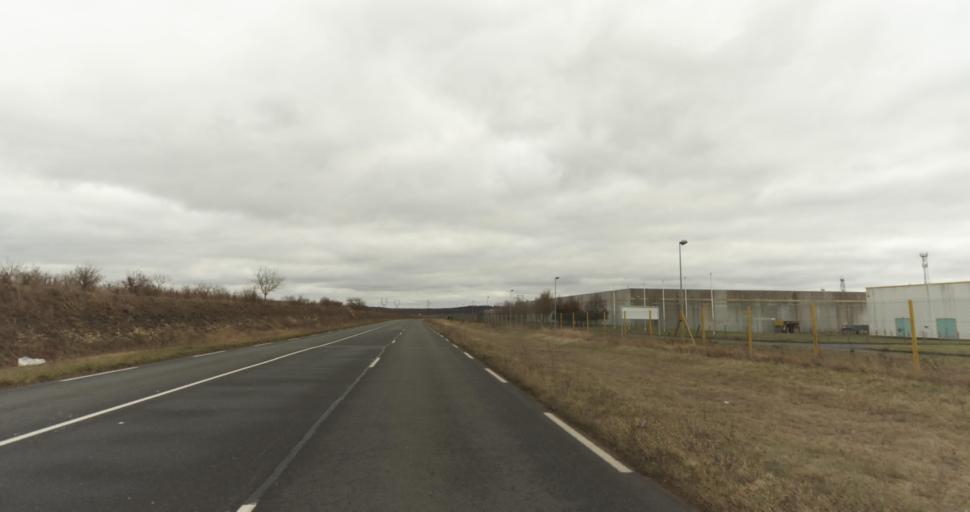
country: FR
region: Pays de la Loire
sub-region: Departement de Maine-et-Loire
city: Varrains
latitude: 47.2111
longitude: -0.0565
